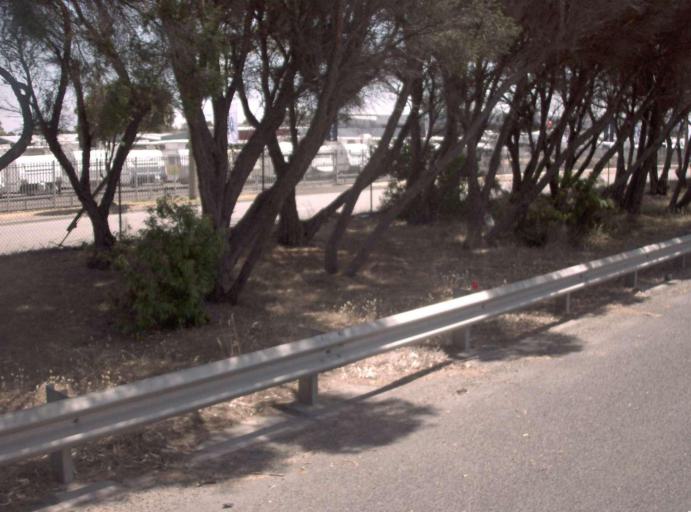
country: AU
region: Victoria
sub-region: Frankston
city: Frankston North
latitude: -38.1154
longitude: 145.1374
